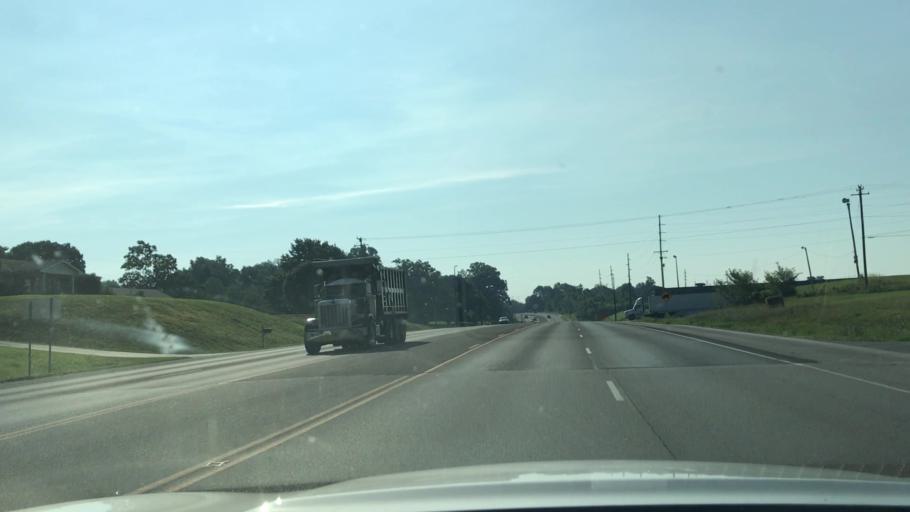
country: US
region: Kentucky
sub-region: Barren County
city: Glasgow
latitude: 37.0117
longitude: -85.9517
